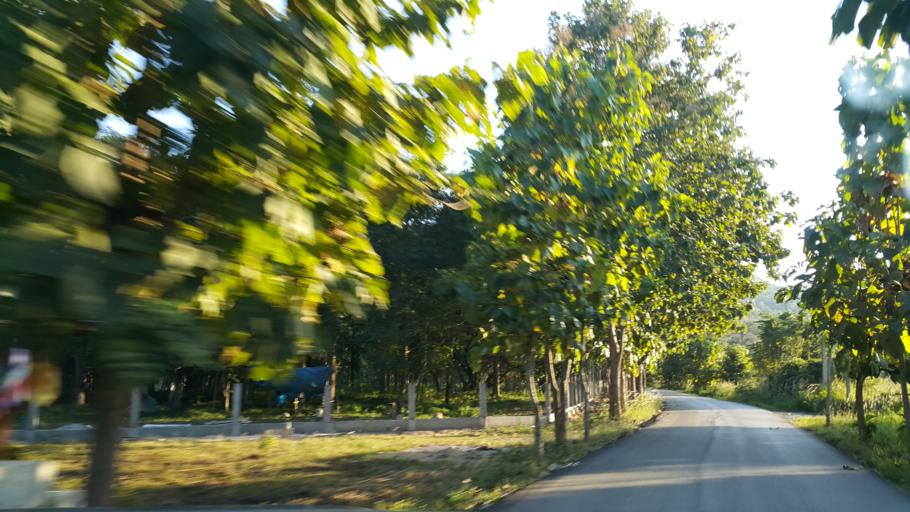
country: TH
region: Chiang Mai
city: Mae On
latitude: 18.7208
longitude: 99.2267
